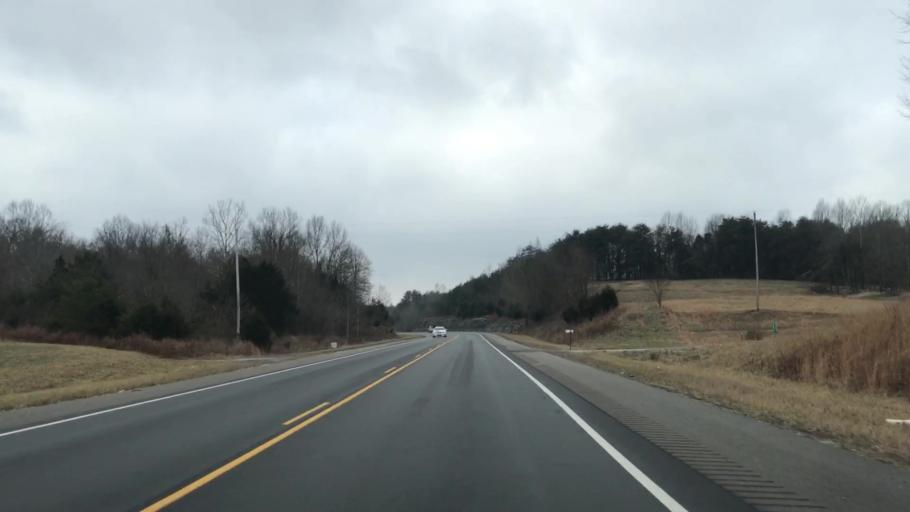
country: US
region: Kentucky
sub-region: Metcalfe County
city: Edmonton
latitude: 36.9527
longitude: -85.4436
